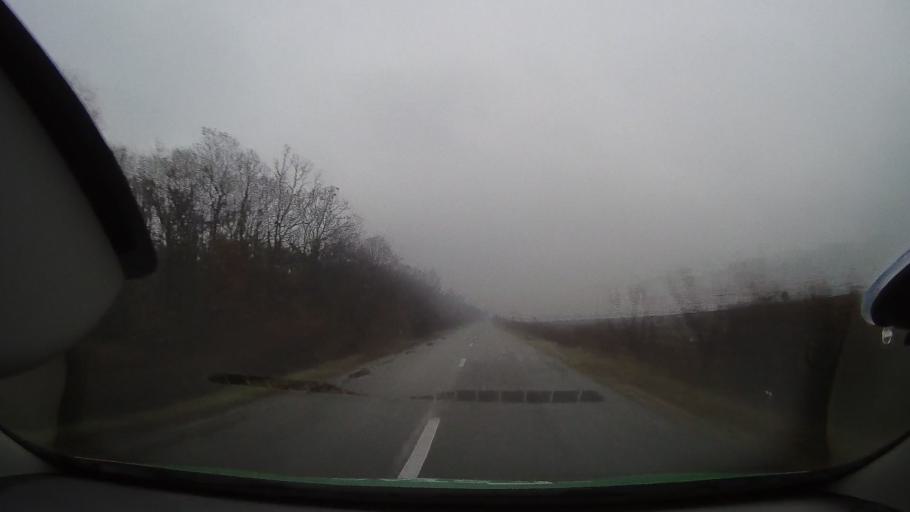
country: RO
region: Bihor
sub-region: Comuna Tinca
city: Gurbediu
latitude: 46.7796
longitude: 21.8741
